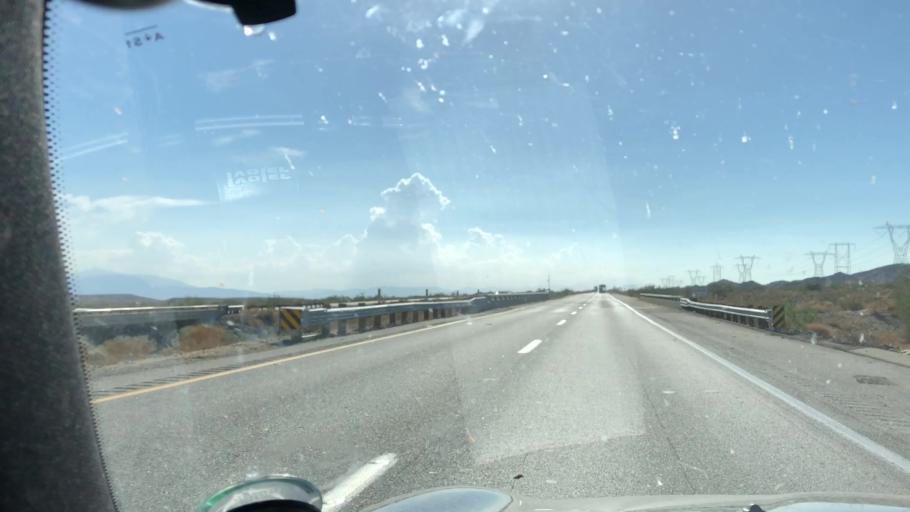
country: US
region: California
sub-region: Riverside County
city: Mecca
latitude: 33.6753
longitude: -115.9448
